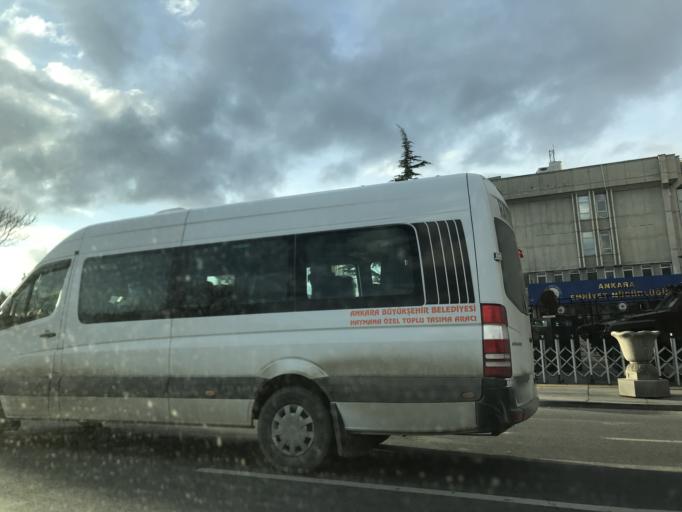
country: TR
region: Ankara
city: Ankara
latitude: 39.9474
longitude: 32.8318
